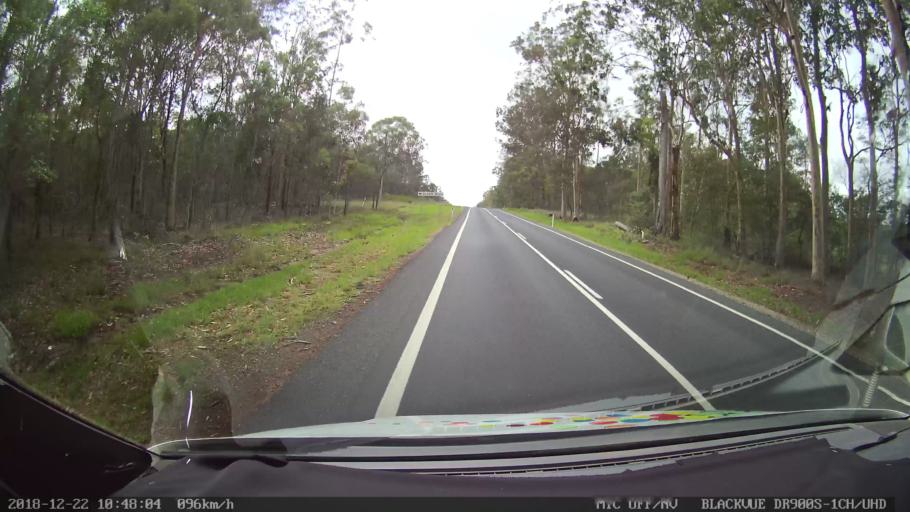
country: AU
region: New South Wales
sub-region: Clarence Valley
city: South Grafton
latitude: -29.6786
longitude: 152.8483
